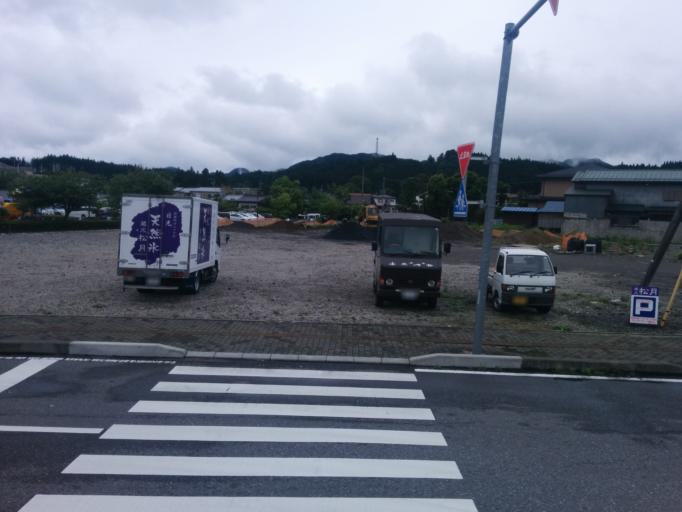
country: JP
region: Tochigi
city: Imaichi
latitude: 36.7221
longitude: 139.6840
